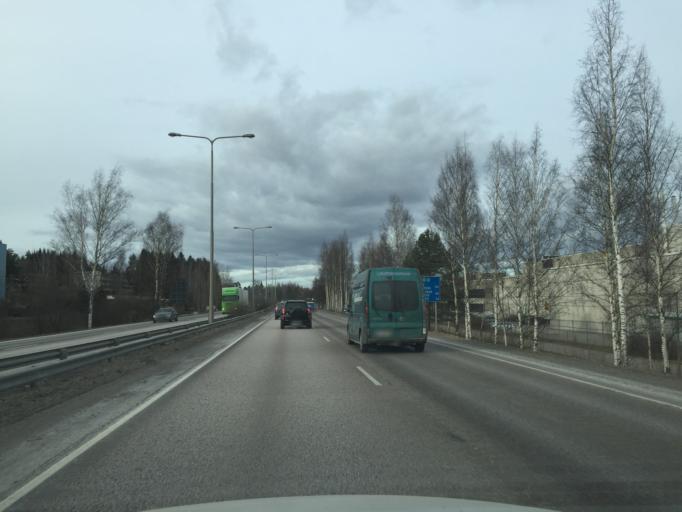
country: FI
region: Uusimaa
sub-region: Helsinki
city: Teekkarikylae
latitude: 60.2677
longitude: 24.8750
